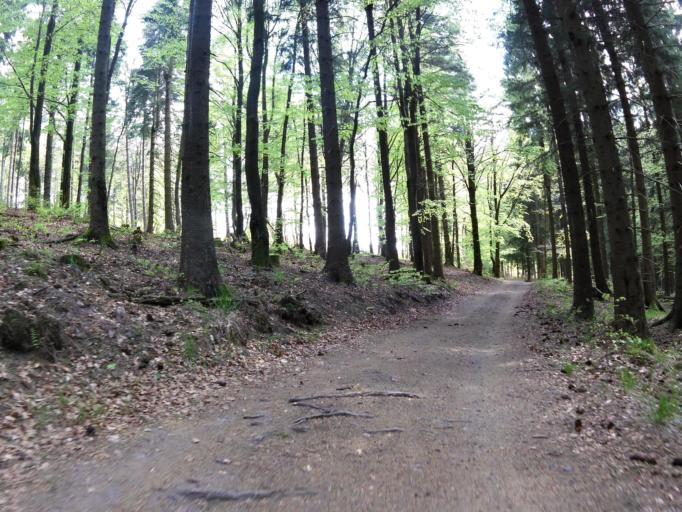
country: DE
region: Thuringia
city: Finsterbergen
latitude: 50.8053
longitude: 10.5452
